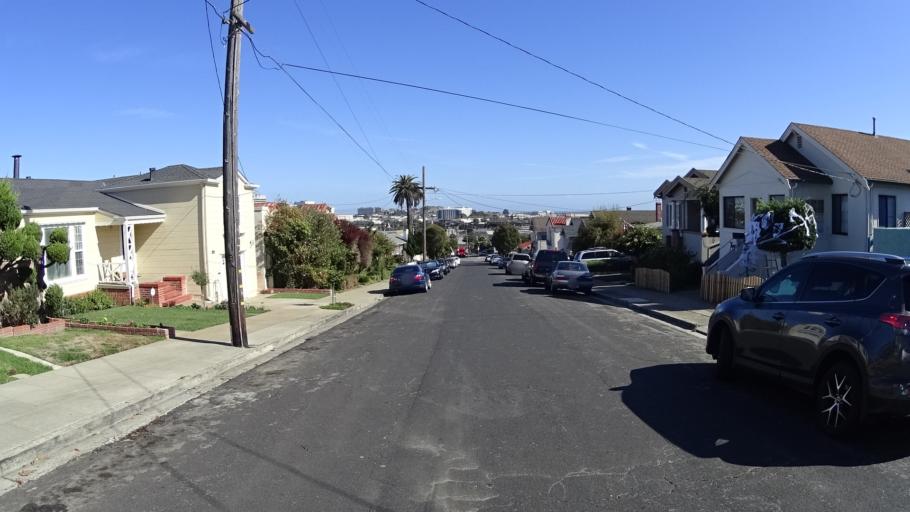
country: US
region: California
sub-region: San Mateo County
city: South San Francisco
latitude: 37.6579
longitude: -122.4133
